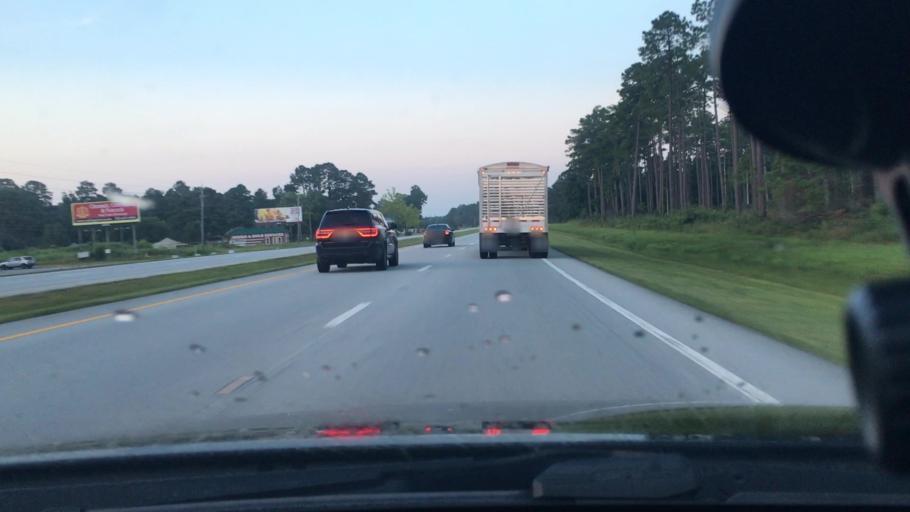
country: US
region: North Carolina
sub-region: Craven County
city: Neuse Forest
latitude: 34.9452
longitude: -76.9486
